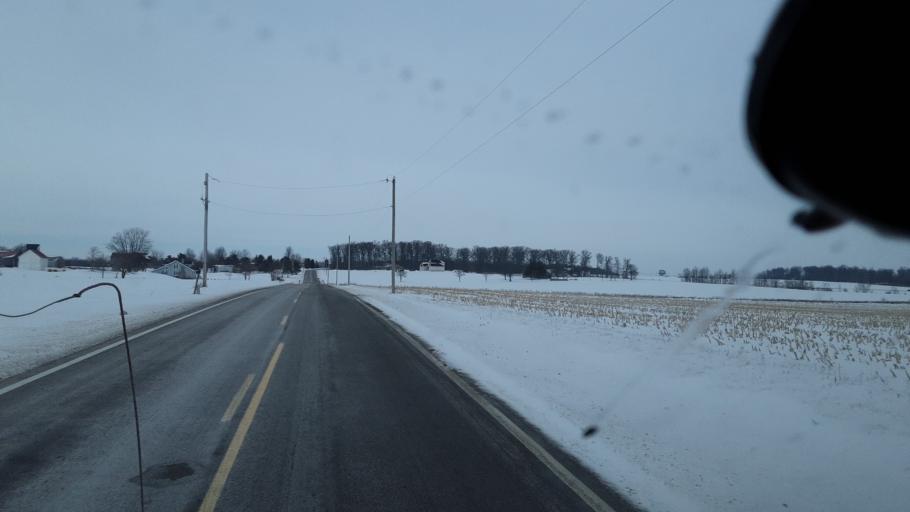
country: US
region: Ohio
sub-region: Union County
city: Marysville
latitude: 40.1757
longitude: -83.3437
